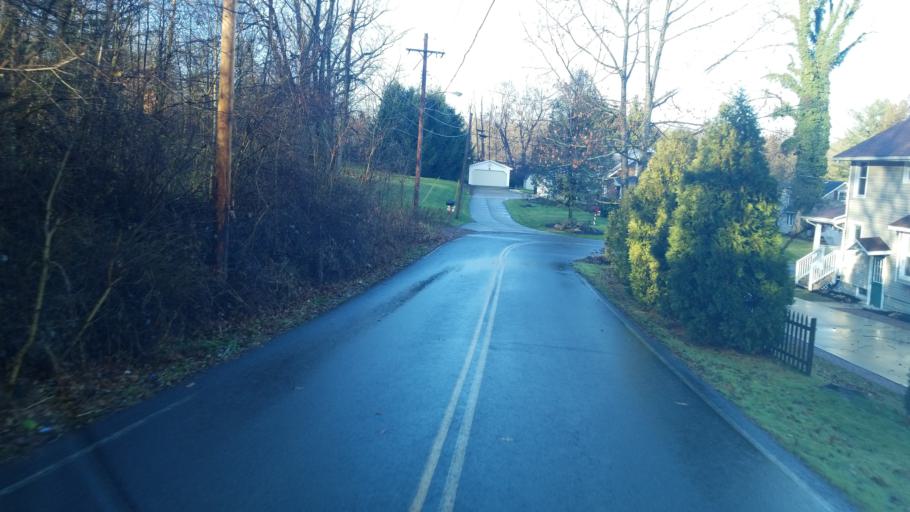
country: US
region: Ohio
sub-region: Richland County
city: Mansfield
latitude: 40.7278
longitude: -82.5030
